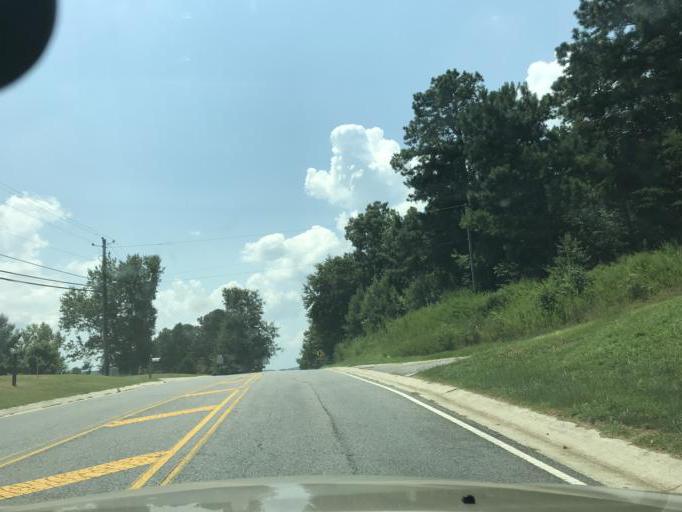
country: US
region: Georgia
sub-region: Forsyth County
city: Cumming
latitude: 34.2830
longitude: -84.1259
